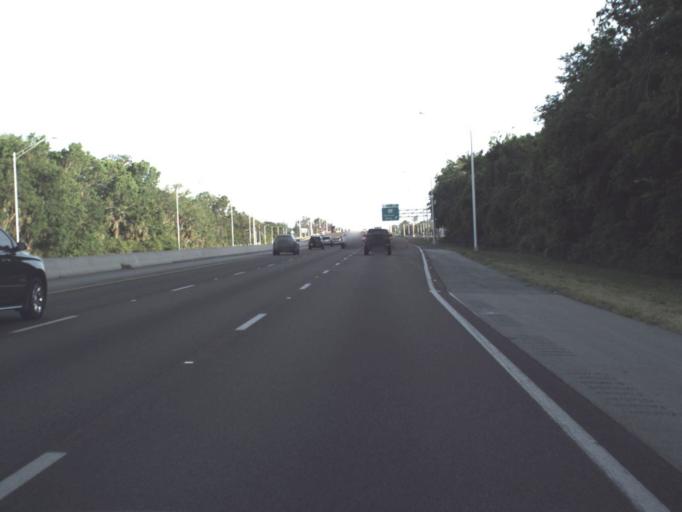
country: US
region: Florida
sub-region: Brevard County
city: Mims
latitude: 28.6729
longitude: -80.8726
